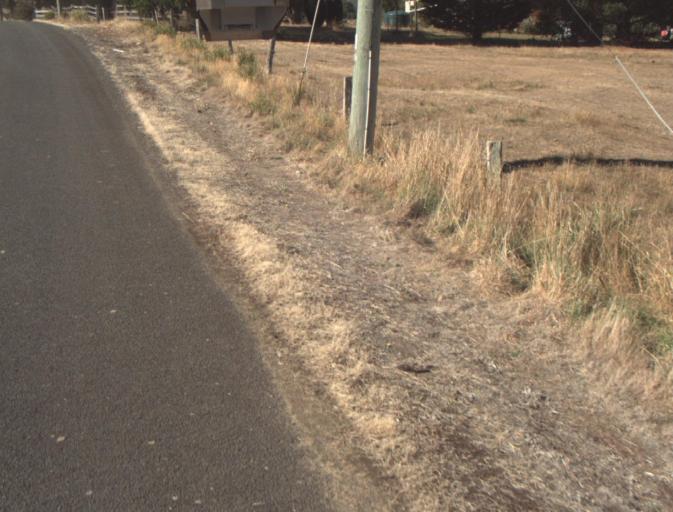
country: AU
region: Tasmania
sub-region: Launceston
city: Newstead
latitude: -41.3079
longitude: 147.3188
